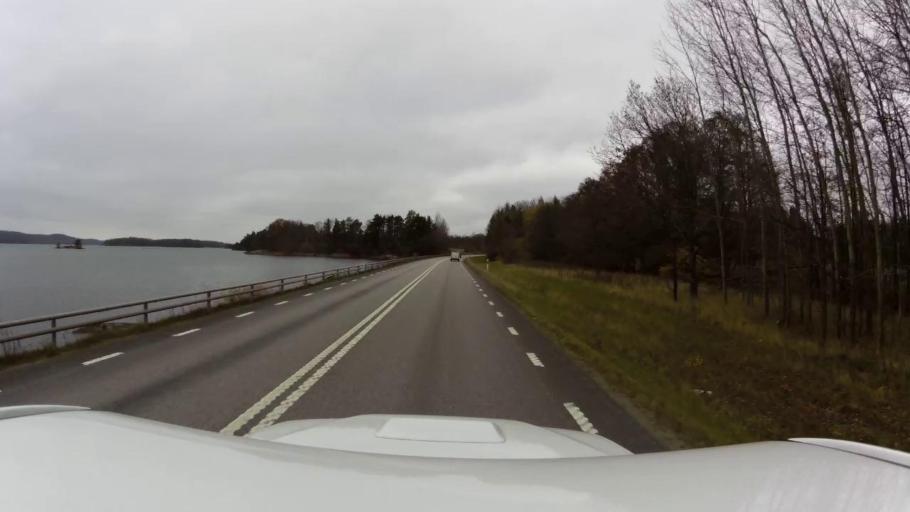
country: SE
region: OEstergoetland
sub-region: Kinda Kommun
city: Rimforsa
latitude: 58.1544
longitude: 15.6799
